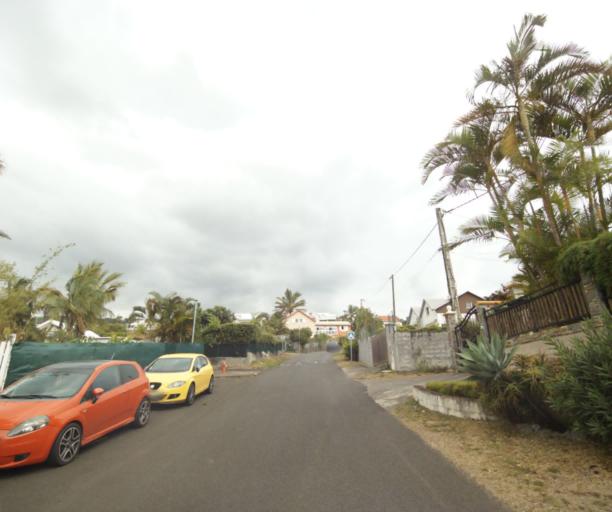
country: RE
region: Reunion
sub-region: Reunion
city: Saint-Paul
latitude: -21.0250
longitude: 55.3058
